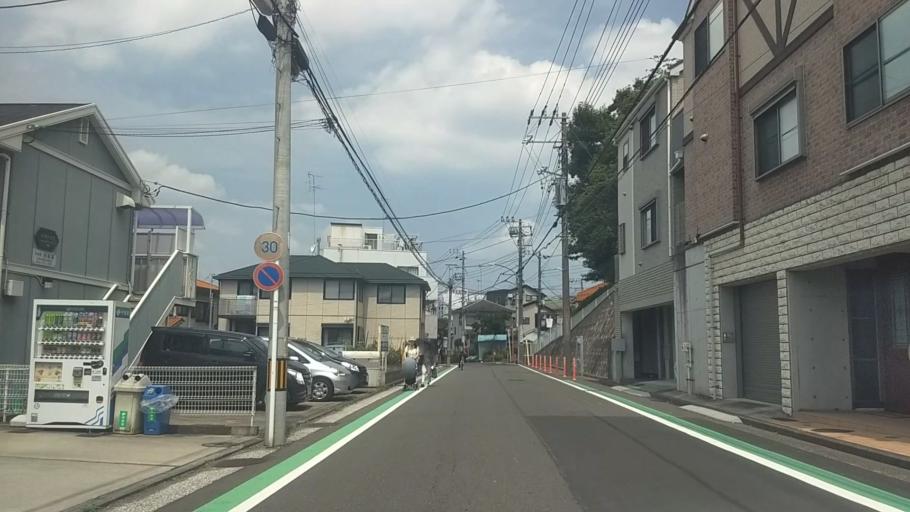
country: JP
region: Kanagawa
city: Yokohama
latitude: 35.5059
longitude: 139.6350
